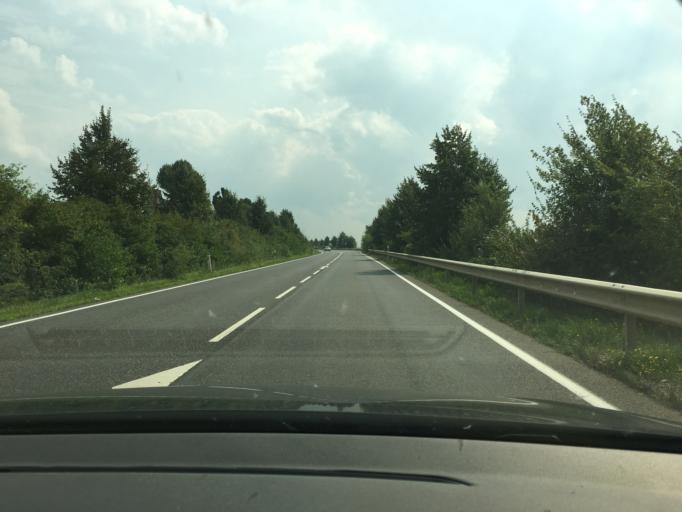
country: DE
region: North Rhine-Westphalia
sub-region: Regierungsbezirk Koln
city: Norvenich
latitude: 50.8353
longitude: 6.6262
